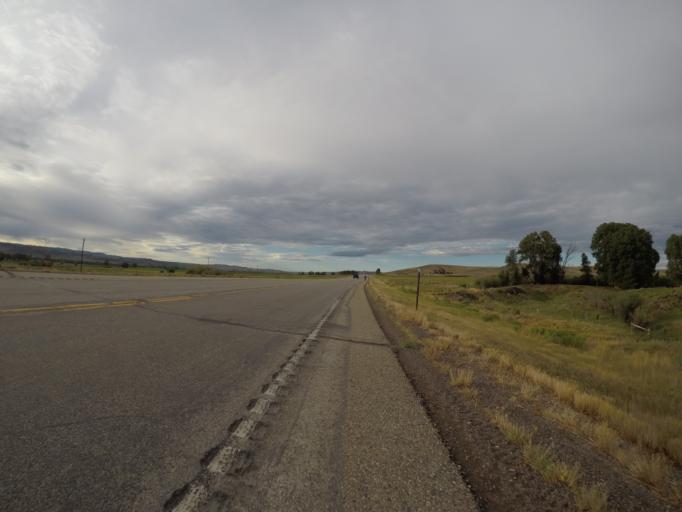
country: US
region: Wyoming
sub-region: Carbon County
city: Saratoga
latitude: 41.3836
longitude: -106.7506
